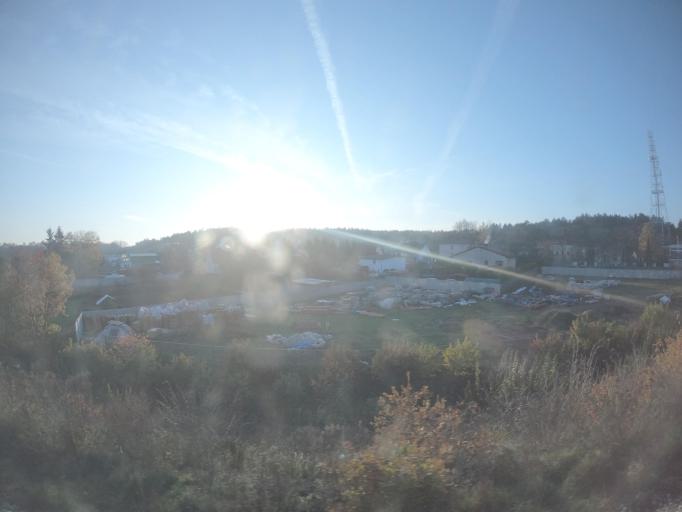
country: PL
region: Lubusz
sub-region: Powiat slubicki
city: Rzepin
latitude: 52.3401
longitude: 14.8298
